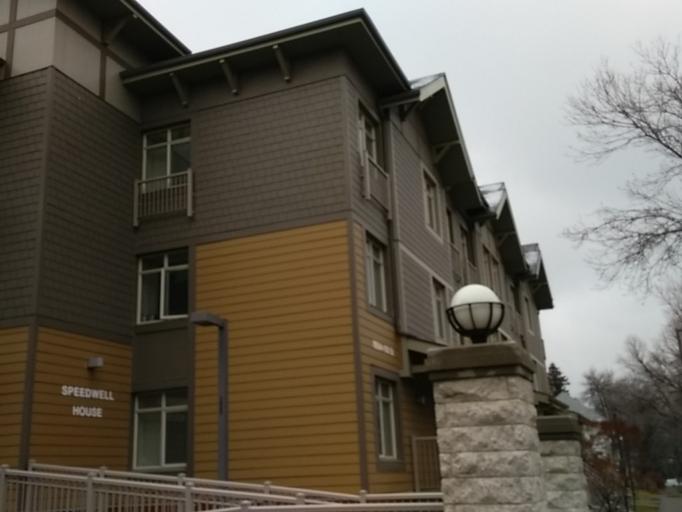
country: CA
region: Alberta
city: Edmonton
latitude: 53.5238
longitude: -113.5152
